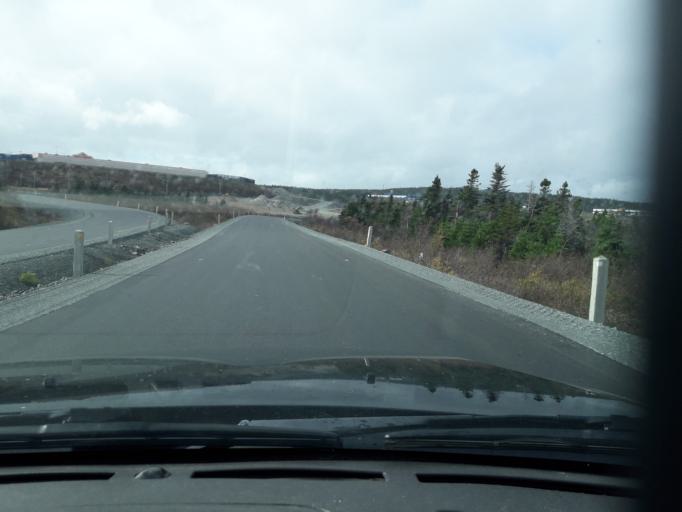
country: CA
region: Newfoundland and Labrador
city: Mount Pearl
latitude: 47.5560
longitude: -52.7737
